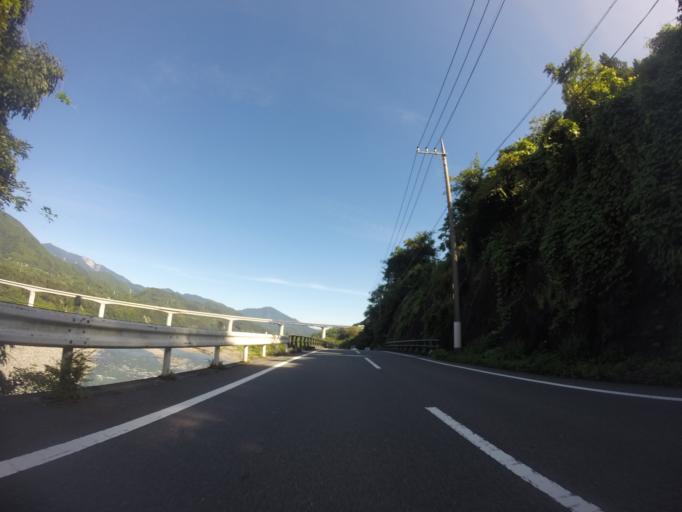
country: JP
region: Shizuoka
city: Fujinomiya
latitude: 35.3090
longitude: 138.4551
